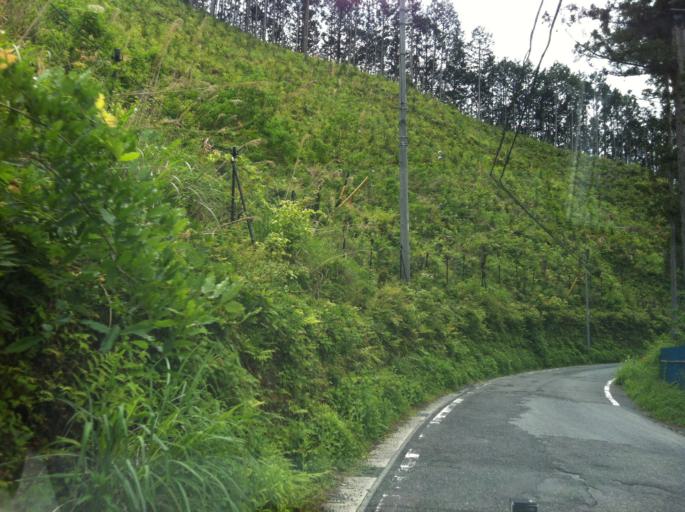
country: JP
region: Shizuoka
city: Shizuoka-shi
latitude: 35.1370
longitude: 138.3275
